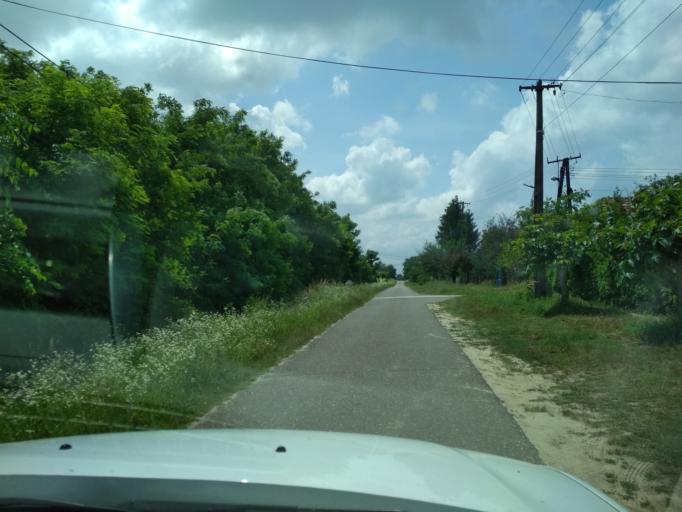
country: HU
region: Pest
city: Tapiosag
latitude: 47.4029
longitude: 19.6382
